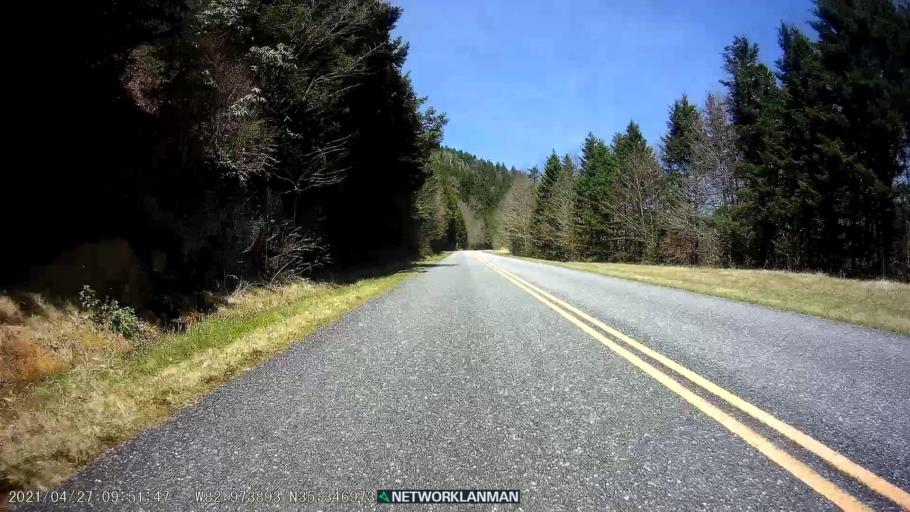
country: US
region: North Carolina
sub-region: Haywood County
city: Hazelwood
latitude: 35.3465
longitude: -82.9735
